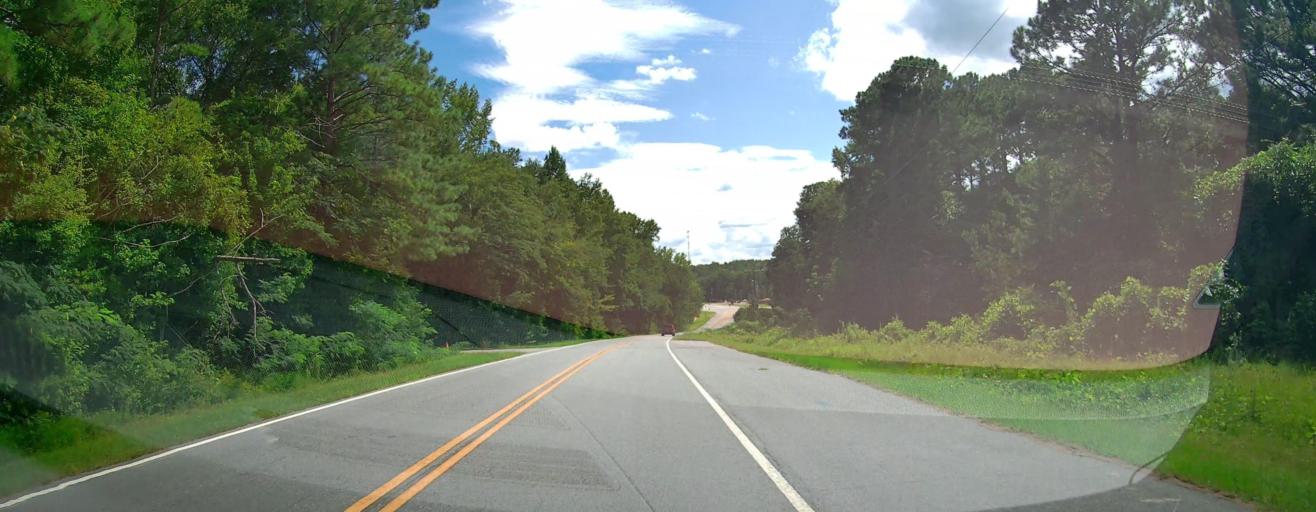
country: US
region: Georgia
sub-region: Chattahoochee County
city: Cusseta
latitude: 32.3037
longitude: -84.7781
